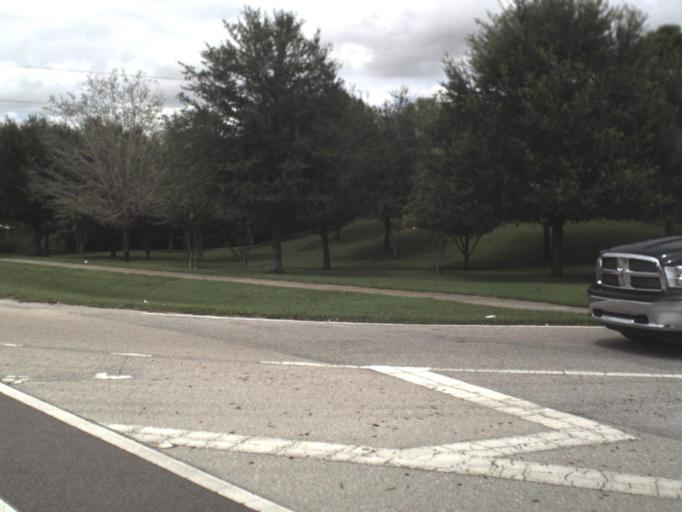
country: US
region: Florida
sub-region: Sarasota County
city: The Meadows
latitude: 27.3884
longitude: -82.4674
